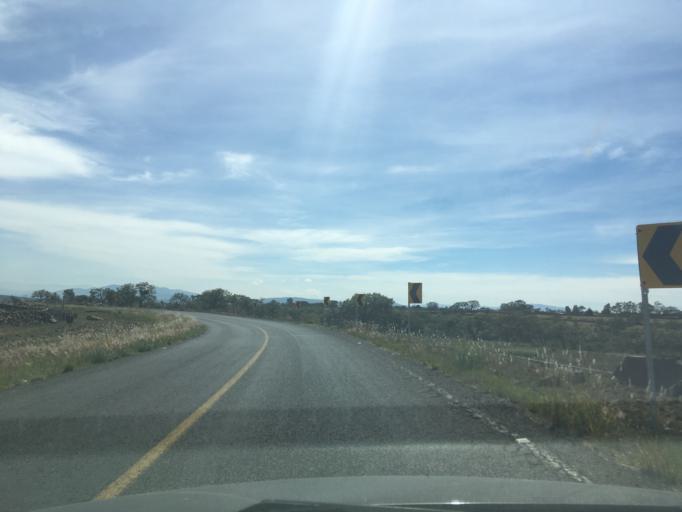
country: MX
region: Queretaro
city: Amealco
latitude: 20.2410
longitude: -100.0806
